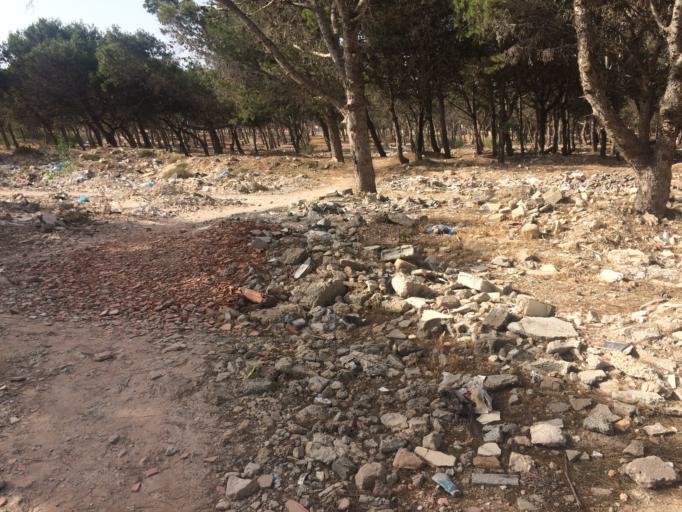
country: MA
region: Doukkala-Abda
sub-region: Safi
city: Safi
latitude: 32.3180
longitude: -9.2325
